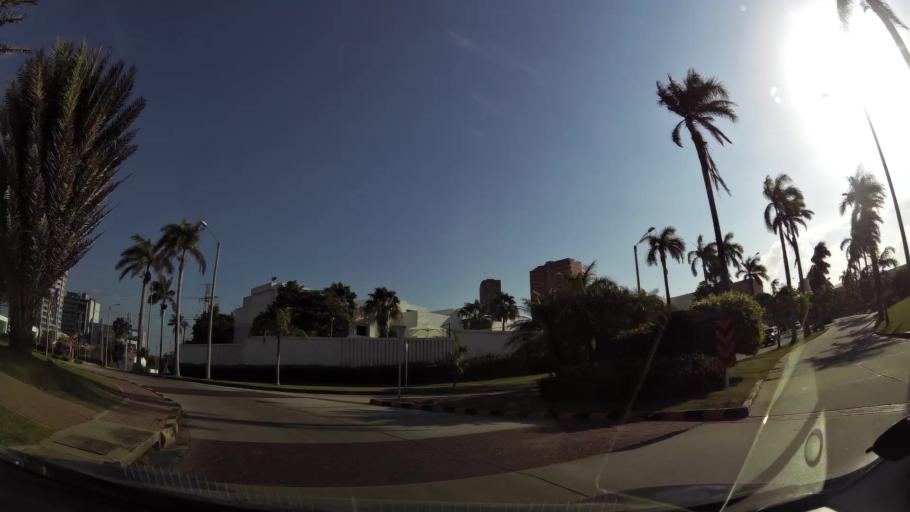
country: CO
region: Atlantico
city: Barranquilla
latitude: 11.0129
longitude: -74.8314
